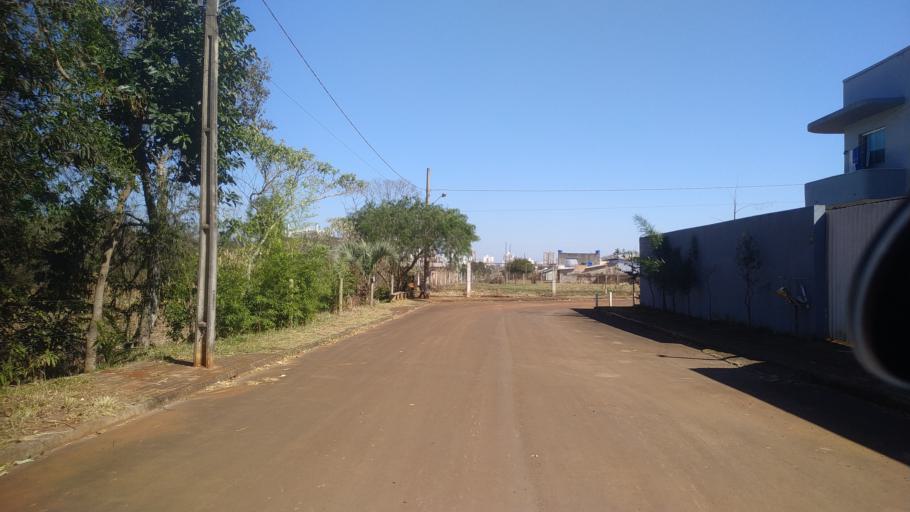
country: BR
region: Santa Catarina
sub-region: Chapeco
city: Chapeco
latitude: -27.0937
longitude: -52.5852
